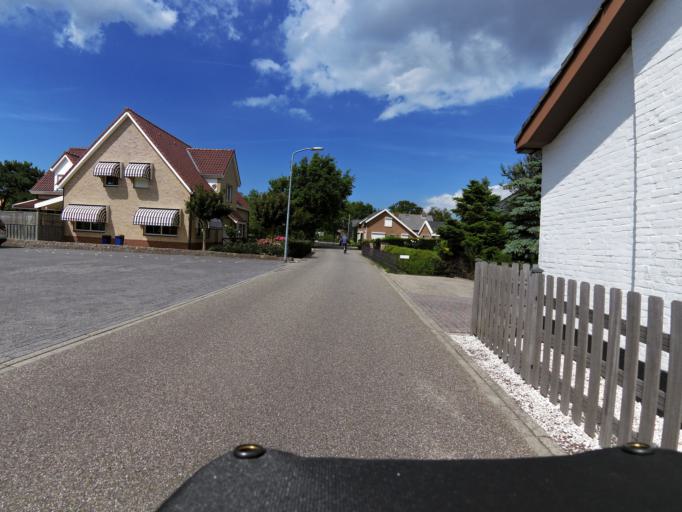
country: NL
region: South Holland
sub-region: Gemeente Goeree-Overflakkee
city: Ouddorp
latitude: 51.8132
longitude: 3.9326
